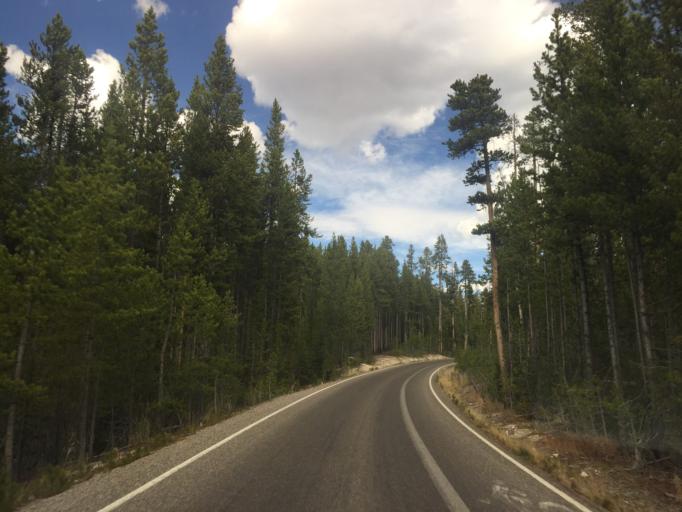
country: US
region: Montana
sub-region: Gallatin County
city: West Yellowstone
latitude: 44.7259
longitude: -110.4840
